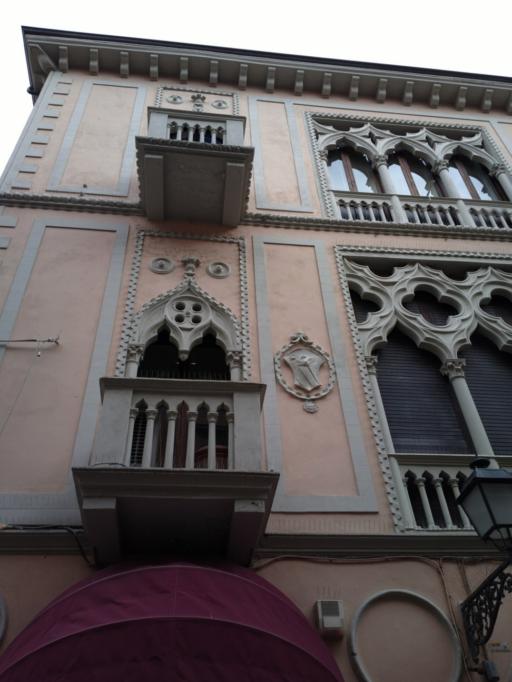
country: IT
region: Tuscany
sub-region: Province of Pisa
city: Pisa
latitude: 43.7129
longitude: 10.4001
